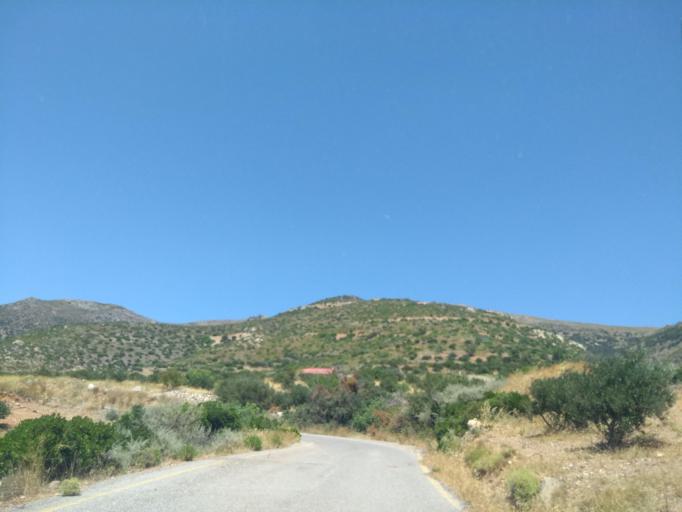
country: GR
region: Crete
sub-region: Nomos Chanias
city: Vryses
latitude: 35.3598
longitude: 23.5480
